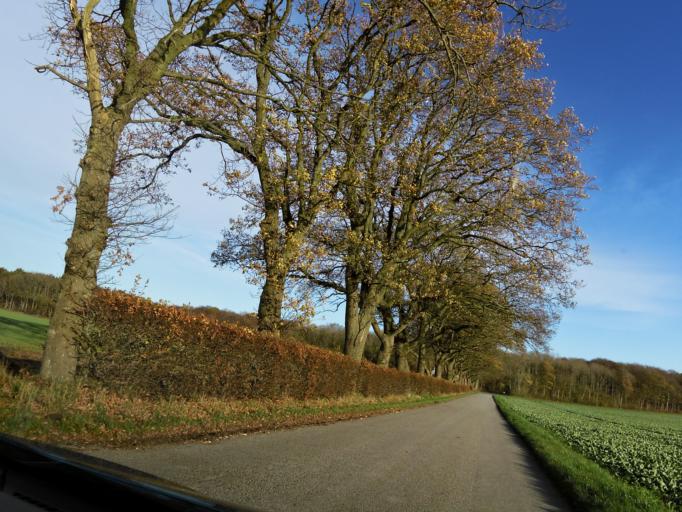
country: DK
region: Central Jutland
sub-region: Odder Kommune
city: Odder
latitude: 55.9144
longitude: 10.2390
